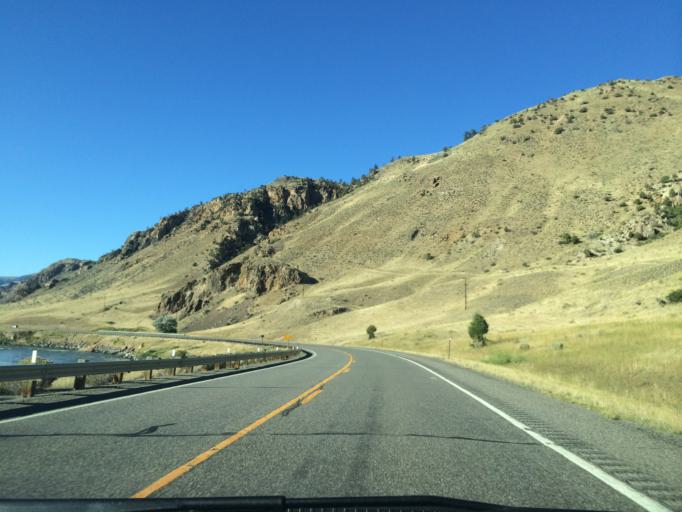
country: US
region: Montana
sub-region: Gallatin County
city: West Yellowstone
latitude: 45.0877
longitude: -110.7749
